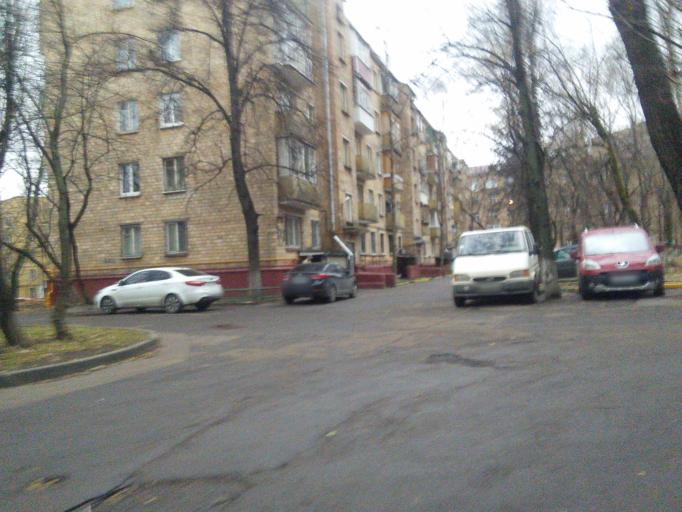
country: RU
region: Moskovskaya
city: Leninskiye Gory
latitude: 55.6957
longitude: 37.5710
